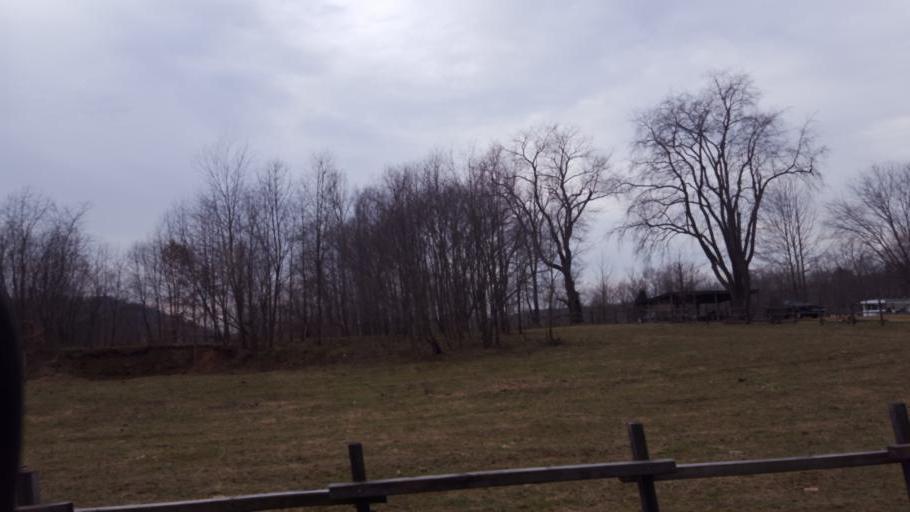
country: US
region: Ohio
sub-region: Ashland County
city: Loudonville
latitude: 40.7007
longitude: -82.2822
